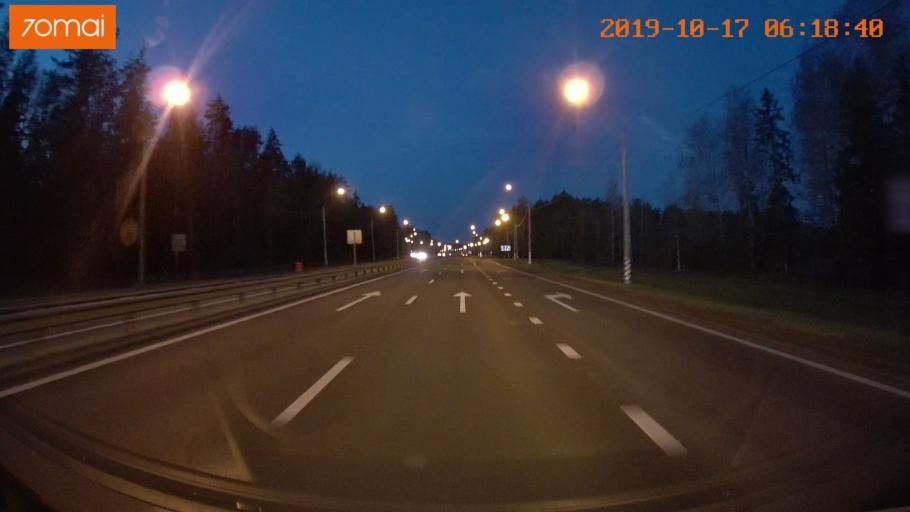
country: RU
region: Ivanovo
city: Lezhnevo
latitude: 56.8391
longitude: 40.9090
